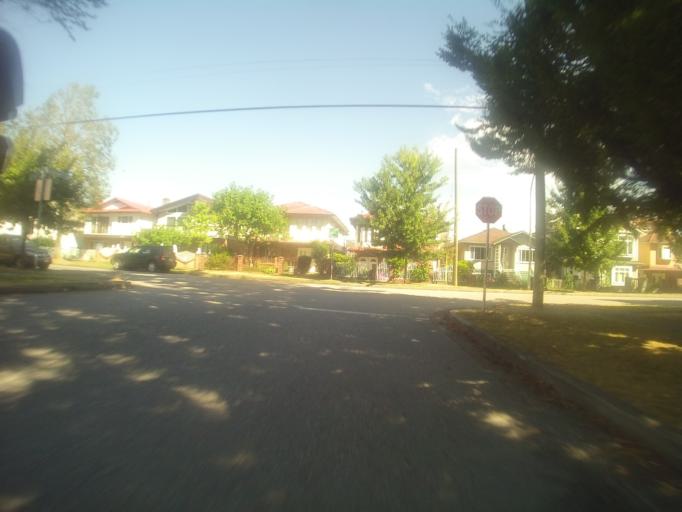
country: CA
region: British Columbia
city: Vancouver
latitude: 49.2386
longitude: -123.0620
